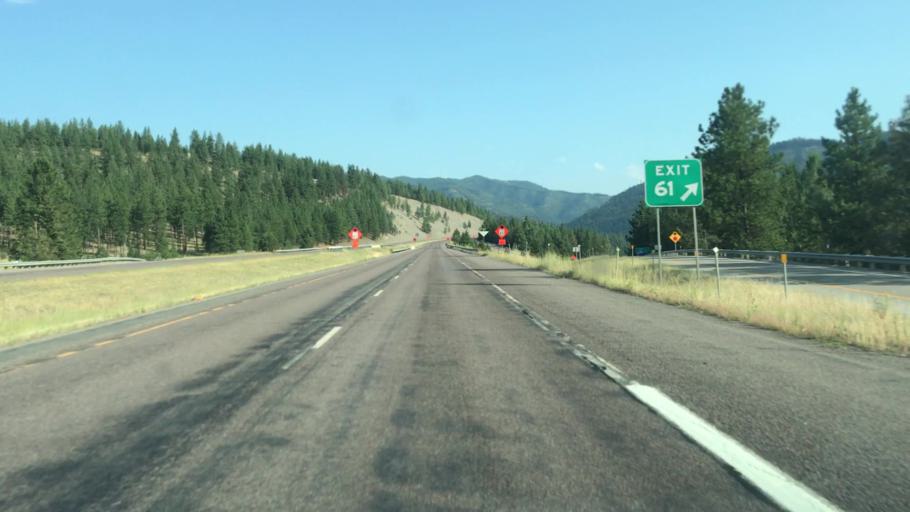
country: US
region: Montana
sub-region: Mineral County
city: Superior
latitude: 47.0280
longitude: -114.7408
